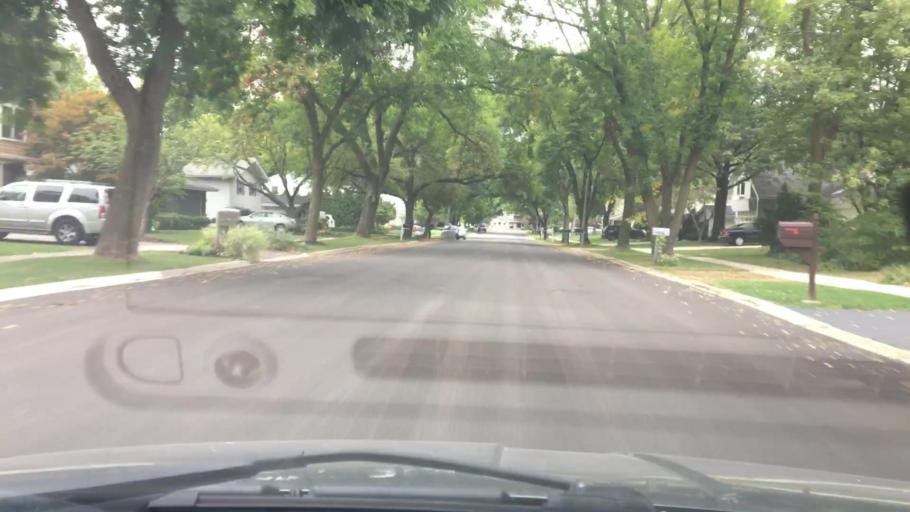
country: US
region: Illinois
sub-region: DuPage County
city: Naperville
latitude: 41.7359
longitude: -88.1363
